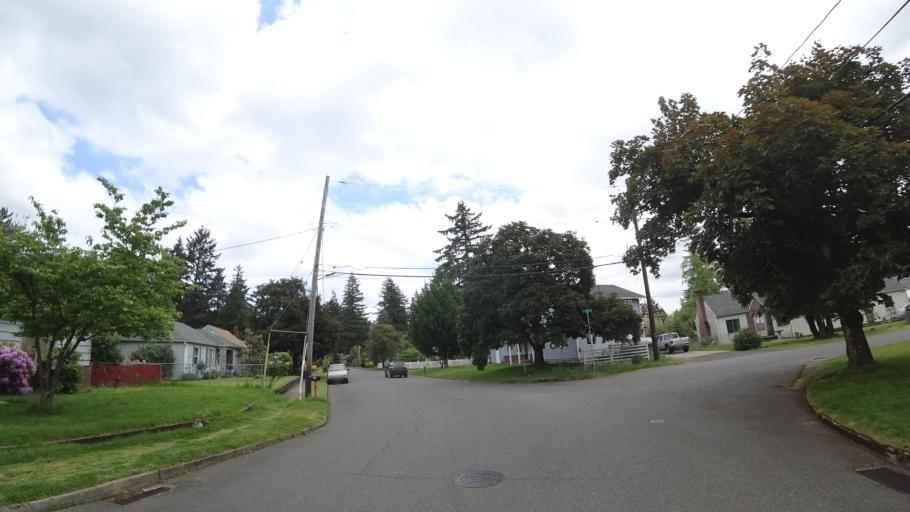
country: US
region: Oregon
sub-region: Multnomah County
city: Lents
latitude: 45.5070
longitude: -122.5358
